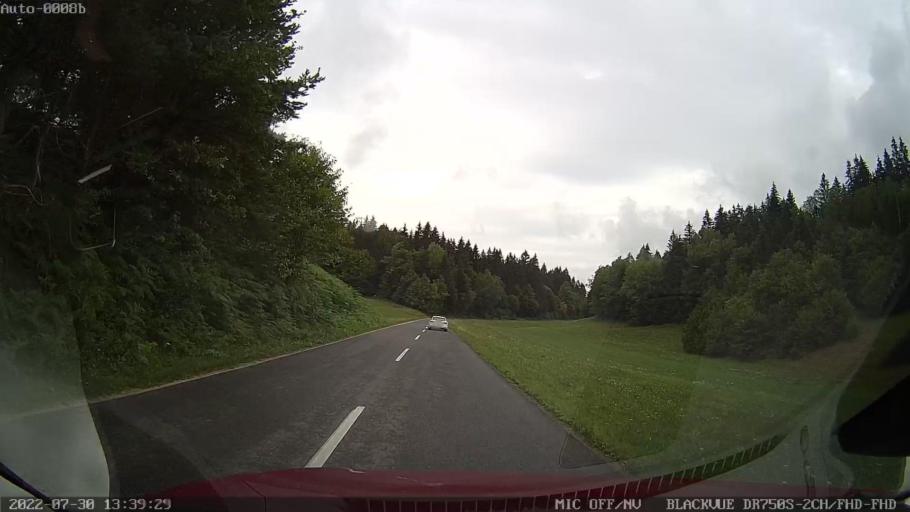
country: SI
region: Zuzemberk
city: Zuzemberk
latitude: 45.8940
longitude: 14.9065
